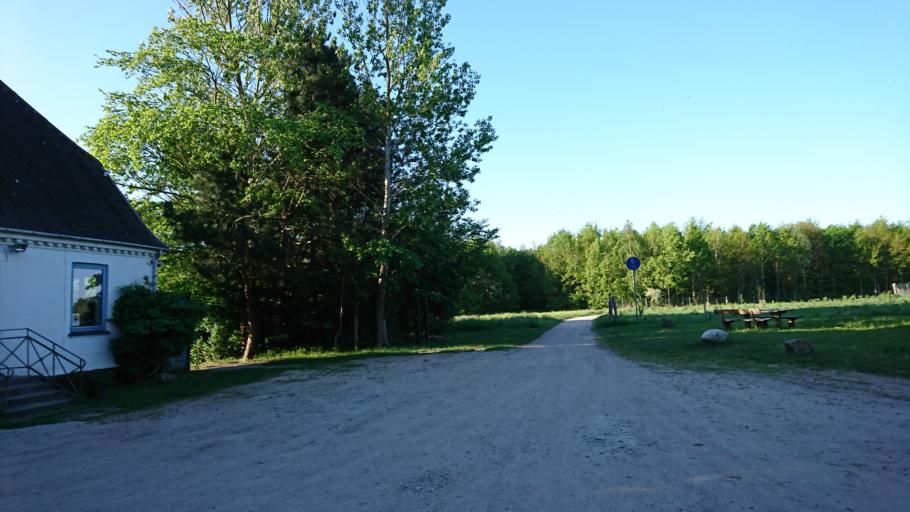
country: DK
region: Capital Region
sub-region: Ballerup Kommune
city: Ballerup
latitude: 55.7127
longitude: 12.3804
